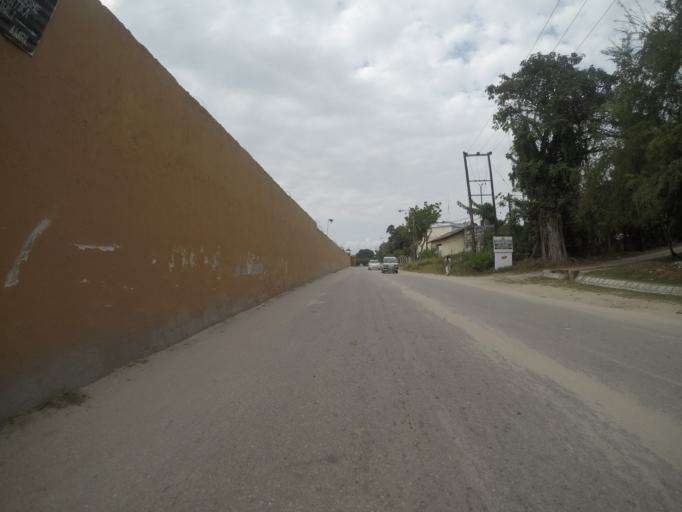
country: TZ
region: Zanzibar Urban/West
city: Zanzibar
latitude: -6.1756
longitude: 39.2029
